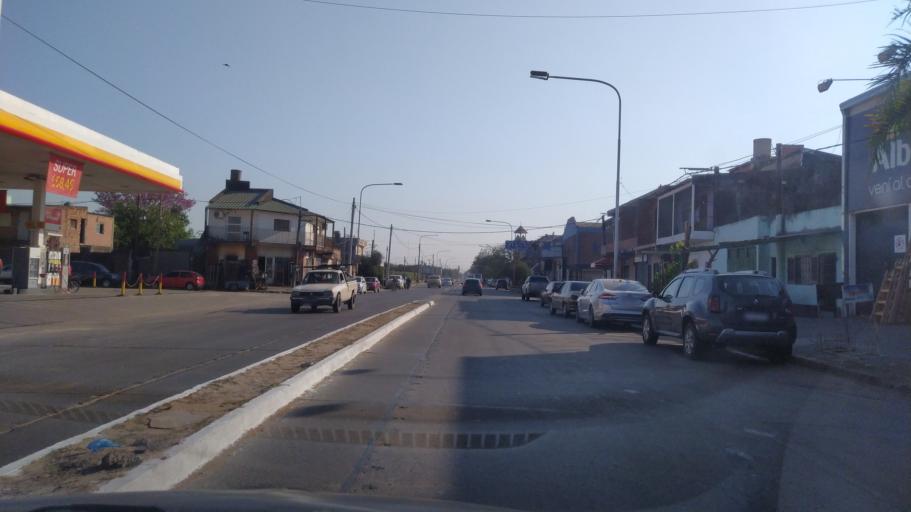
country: AR
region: Corrientes
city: Corrientes
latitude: -27.4861
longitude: -58.8161
